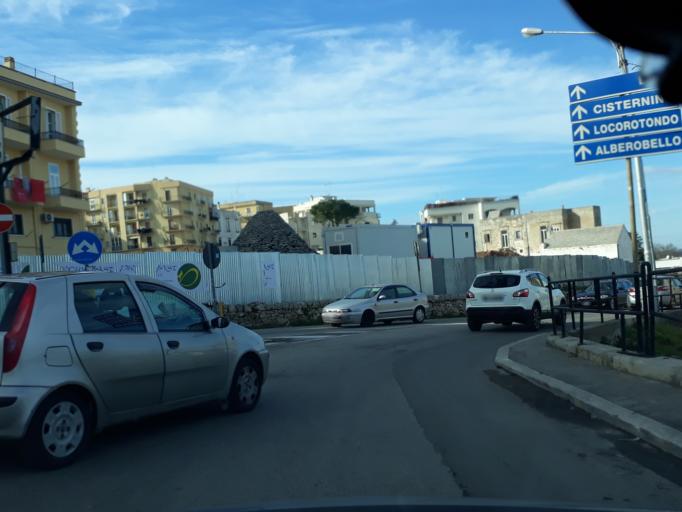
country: IT
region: Apulia
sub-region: Provincia di Taranto
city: Martina Franca
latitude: 40.7071
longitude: 17.3390
